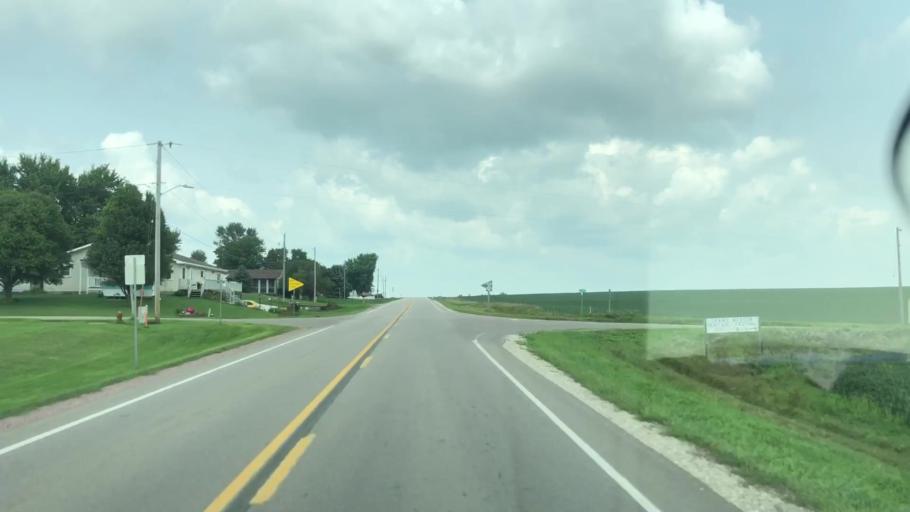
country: US
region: Iowa
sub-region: Plymouth County
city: Kingsley
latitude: 42.5895
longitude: -95.9574
